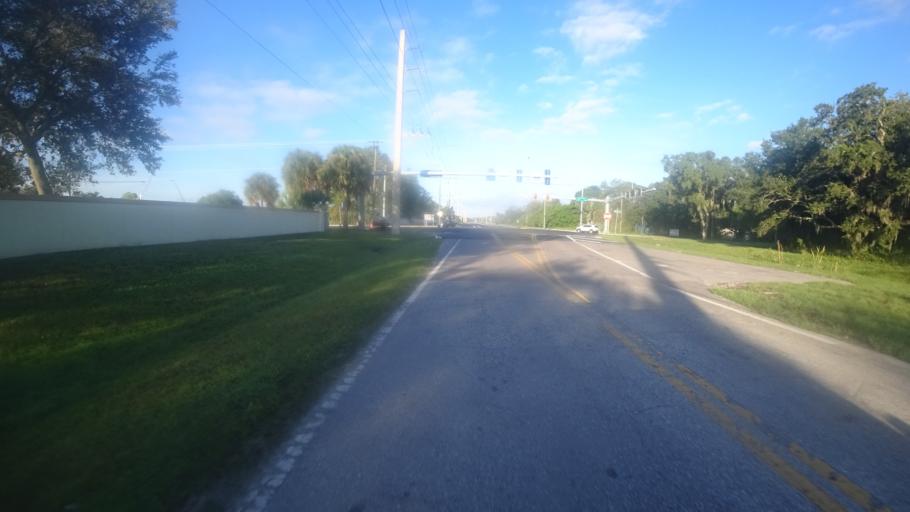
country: US
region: Florida
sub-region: Manatee County
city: Samoset
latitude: 27.4618
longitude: -82.5050
